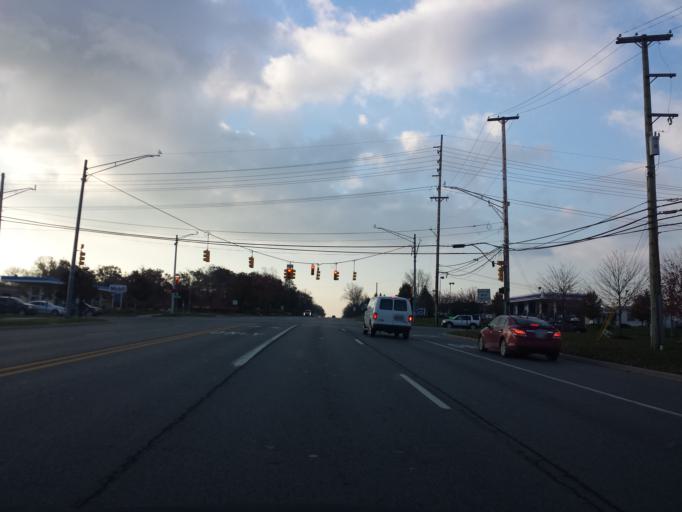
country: US
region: Michigan
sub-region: Oakland County
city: Bloomfield Hills
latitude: 42.6205
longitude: -83.2487
